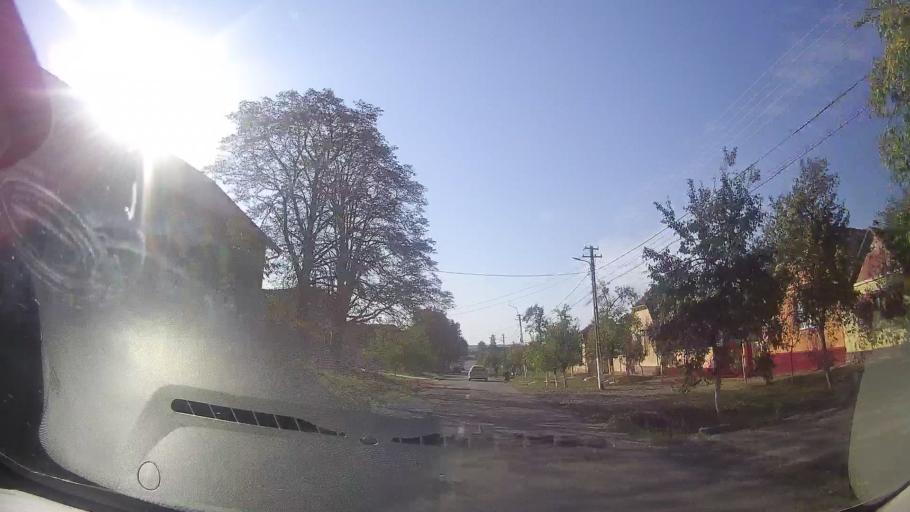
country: RO
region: Timis
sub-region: Oras Recas
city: Recas
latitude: 45.8619
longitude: 21.5150
